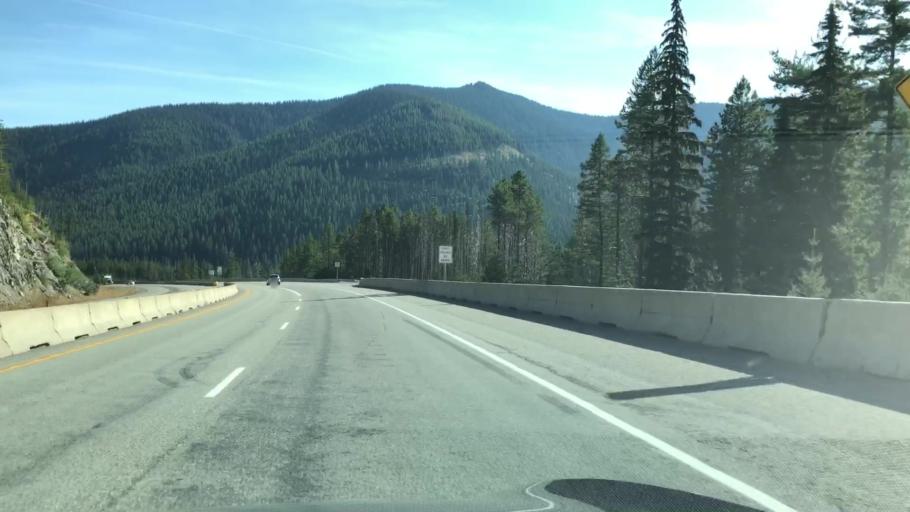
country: US
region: Idaho
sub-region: Shoshone County
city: Wallace
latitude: 47.4489
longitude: -115.6938
